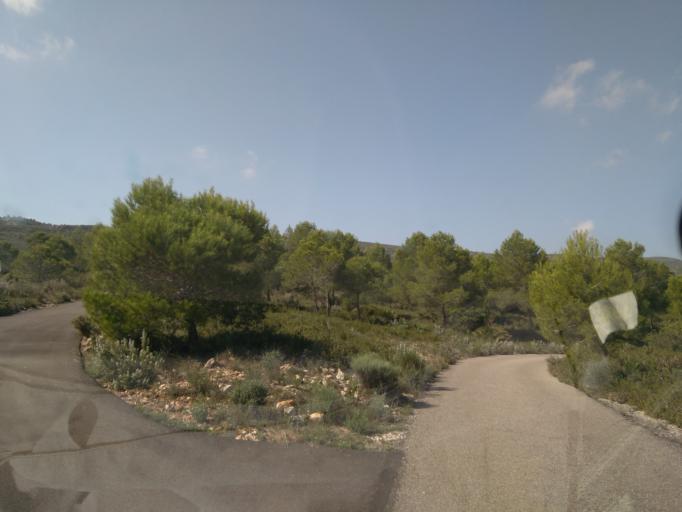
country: ES
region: Valencia
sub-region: Provincia de Valencia
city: Tous
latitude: 39.1821
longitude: -0.6334
